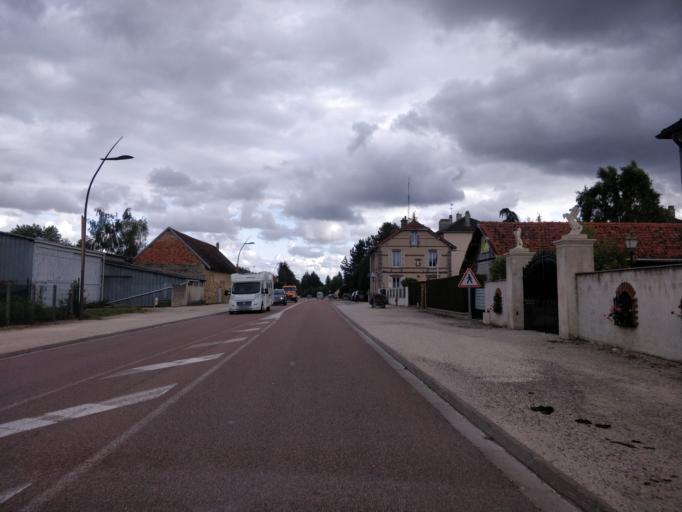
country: FR
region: Champagne-Ardenne
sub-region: Departement de l'Aube
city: Lusigny-sur-Barse
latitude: 48.2509
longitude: 4.2642
